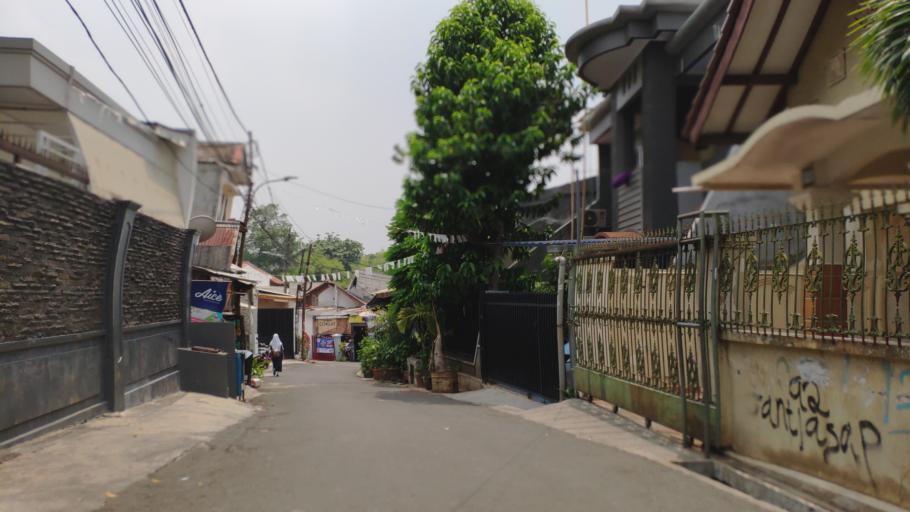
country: ID
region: Banten
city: South Tangerang
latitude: -6.2679
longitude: 106.7764
